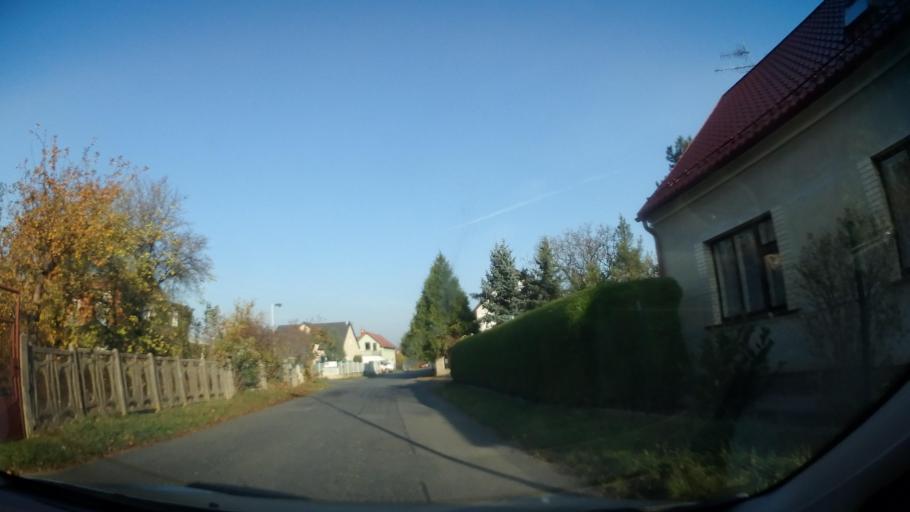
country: CZ
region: Central Bohemia
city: Sestajovice
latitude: 50.0716
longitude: 14.6750
